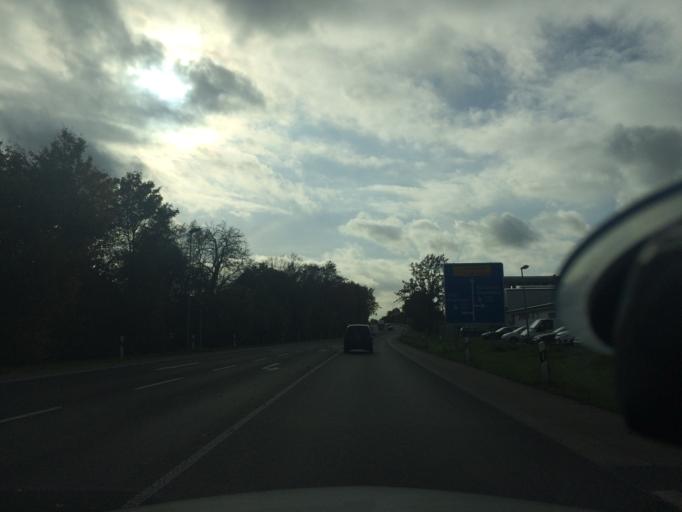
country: DE
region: Hesse
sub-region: Regierungsbezirk Darmstadt
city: Gross-Gerau
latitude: 49.9345
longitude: 8.4923
